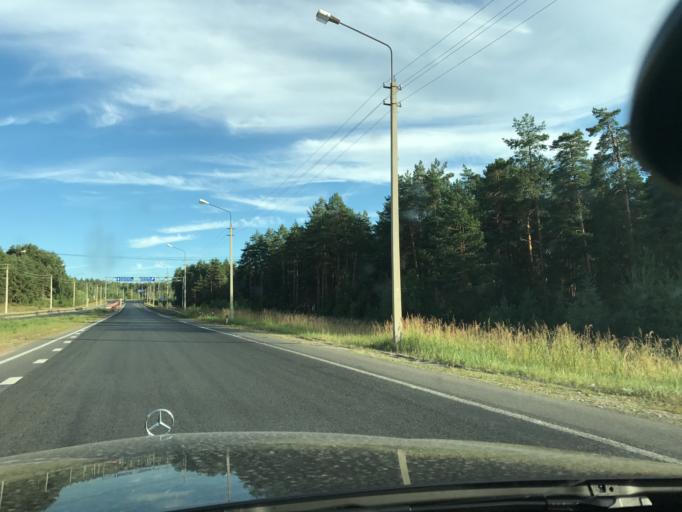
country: RU
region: Vladimir
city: Kommunar
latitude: 56.0622
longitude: 40.4344
